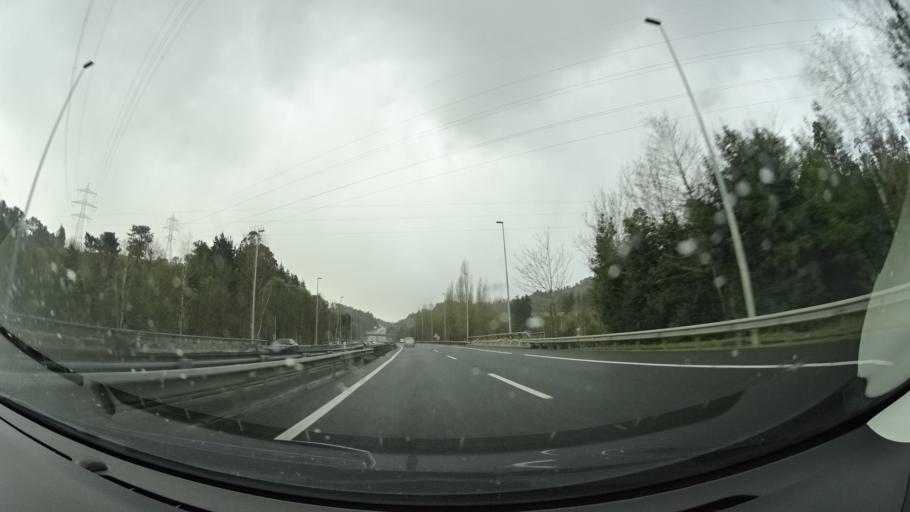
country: ES
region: Basque Country
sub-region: Bizkaia
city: Derio
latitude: 43.3327
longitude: -2.8693
